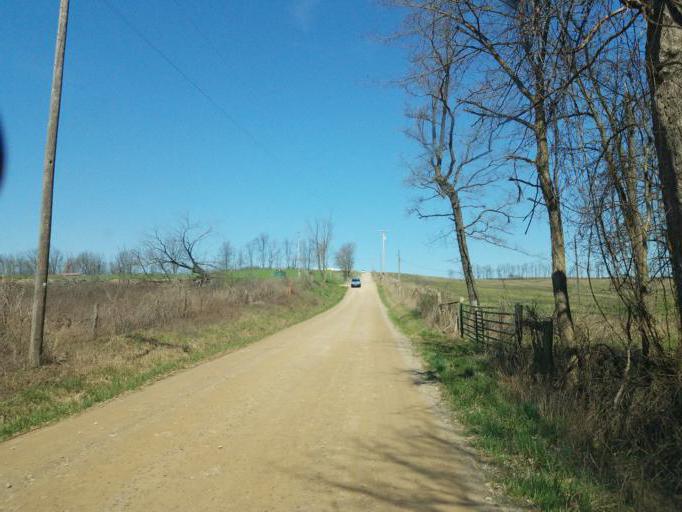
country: US
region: Ohio
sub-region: Knox County
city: Oak Hill
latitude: 40.3306
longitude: -82.1911
